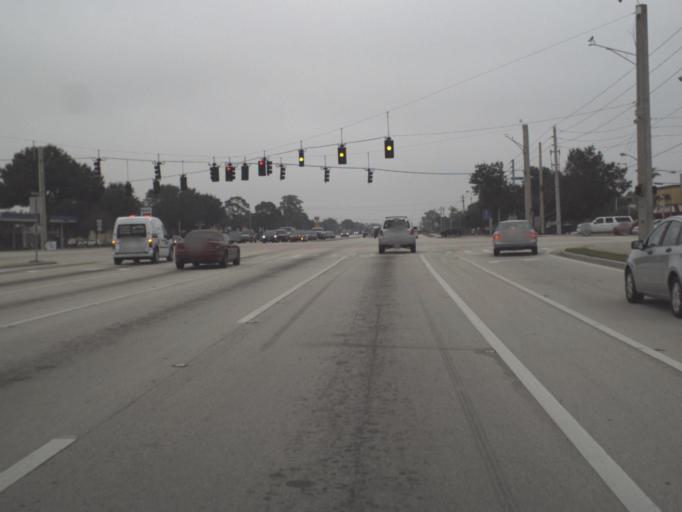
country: US
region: Florida
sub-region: Brevard County
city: Palm Bay
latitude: 28.0351
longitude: -80.6226
